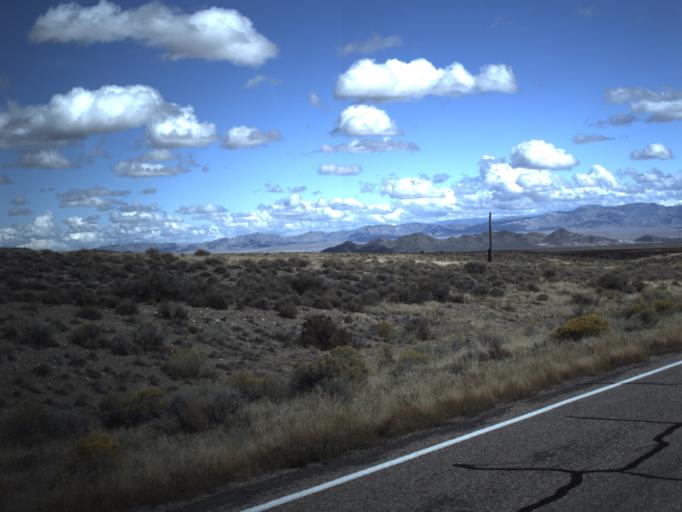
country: US
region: Utah
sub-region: Beaver County
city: Milford
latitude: 38.4495
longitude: -113.1951
